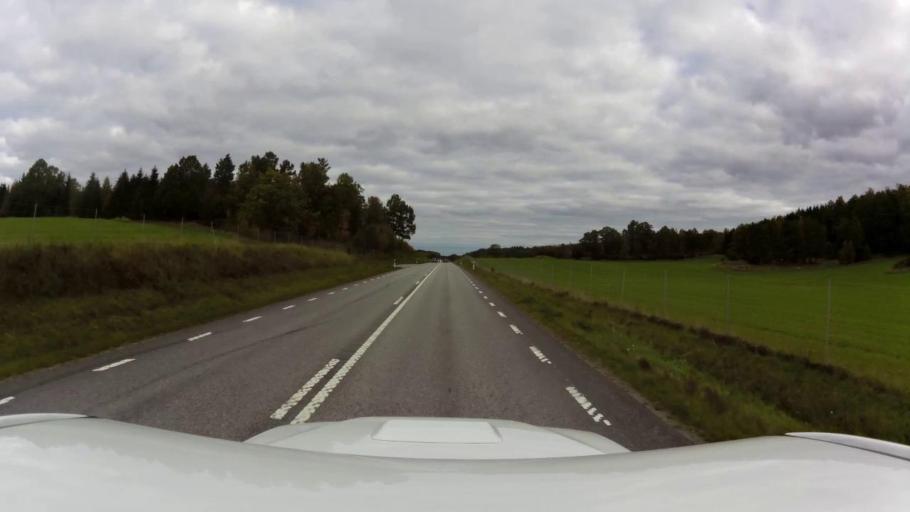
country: SE
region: OEstergoetland
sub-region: Kinda Kommun
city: Rimforsa
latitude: 58.1928
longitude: 15.6668
